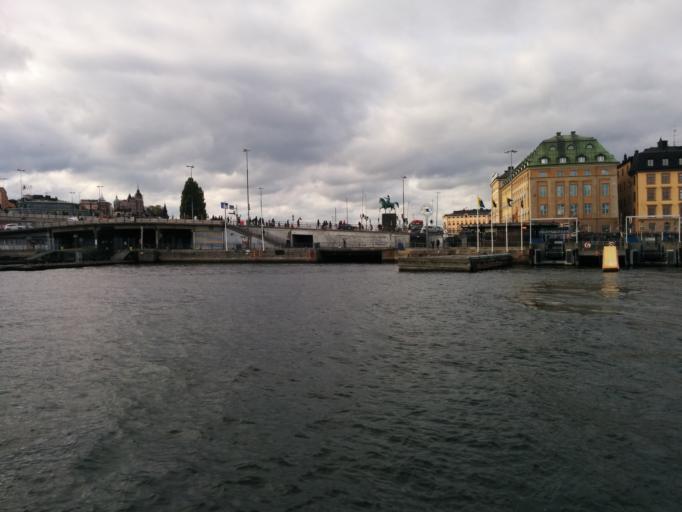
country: SE
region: Stockholm
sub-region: Stockholms Kommun
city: Stockholm
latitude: 59.3215
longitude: 18.0757
